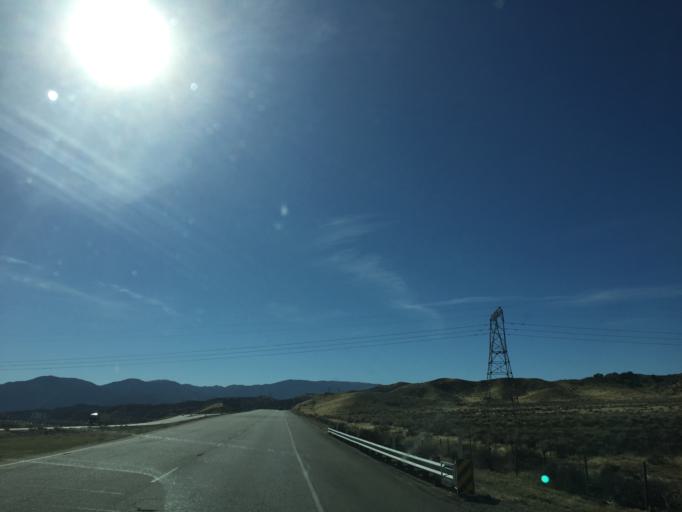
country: US
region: California
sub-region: Kern County
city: Lebec
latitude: 34.7722
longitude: -118.7796
